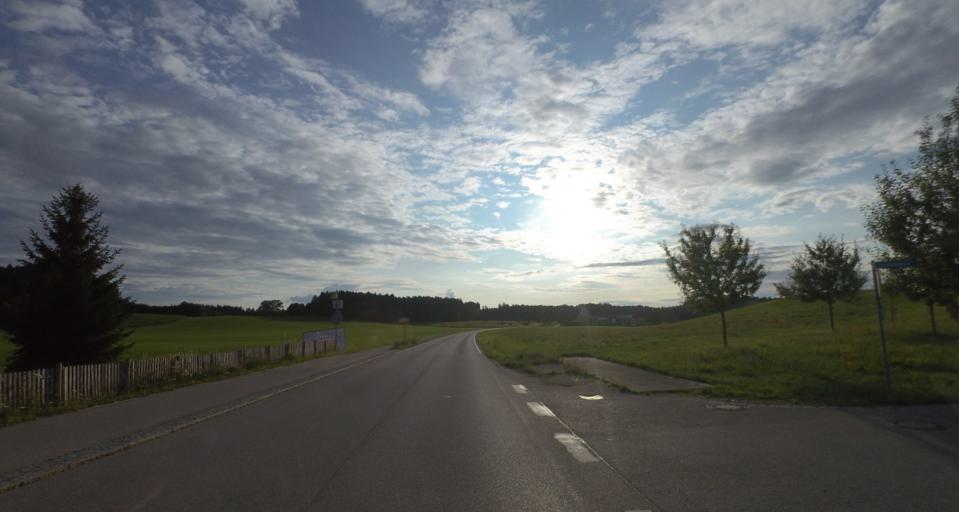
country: DE
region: Bavaria
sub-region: Upper Bavaria
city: Nussdorf
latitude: 47.9080
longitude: 12.5884
